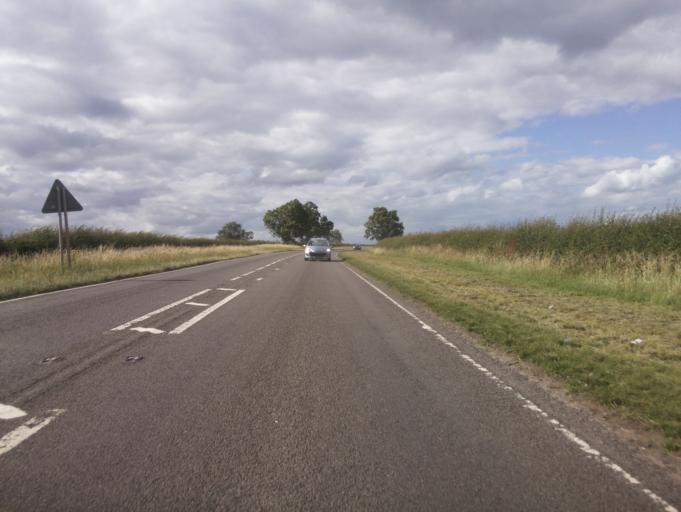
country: GB
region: England
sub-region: Warwickshire
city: Hartshill
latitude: 52.5850
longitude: -1.4788
